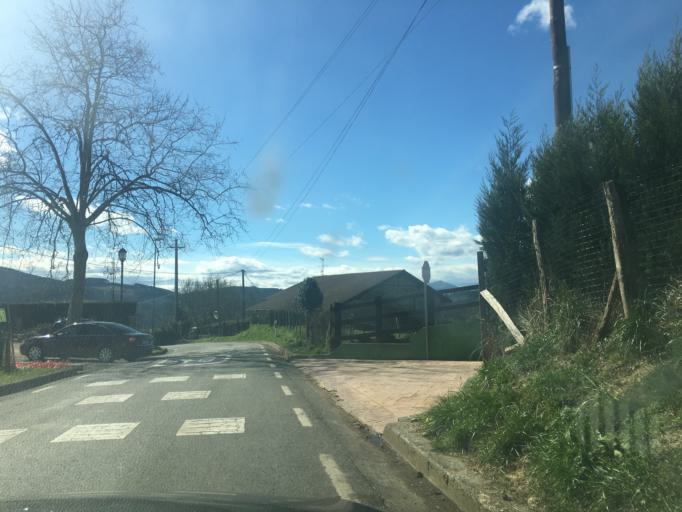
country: ES
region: Basque Country
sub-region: Bizkaia
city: Amorebieta
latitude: 43.2405
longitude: -2.7495
